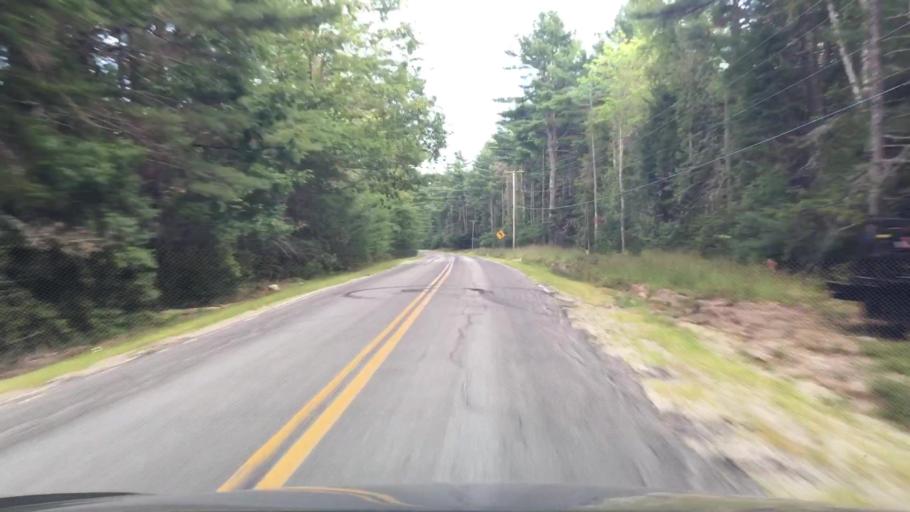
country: US
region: Maine
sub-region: Hancock County
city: Surry
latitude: 44.5094
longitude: -68.5979
